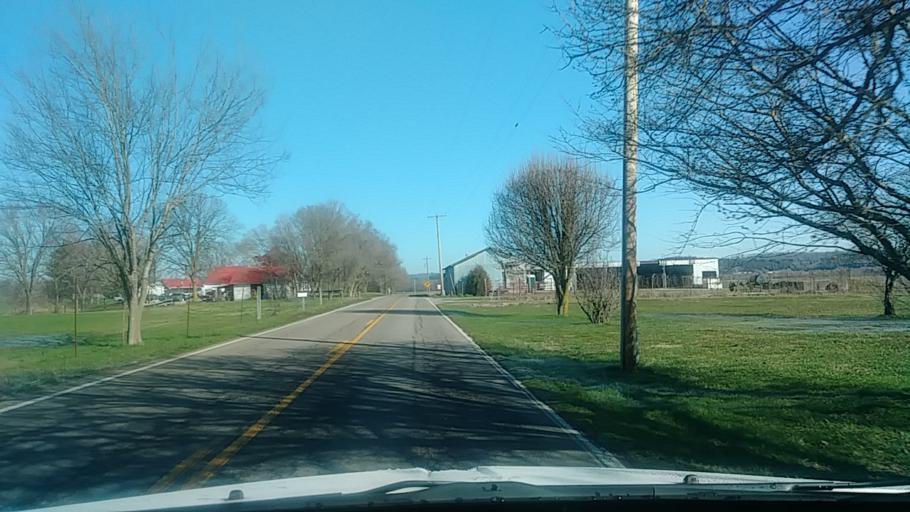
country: US
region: Tennessee
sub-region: Jefferson County
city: White Pine
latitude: 36.1613
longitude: -83.1625
